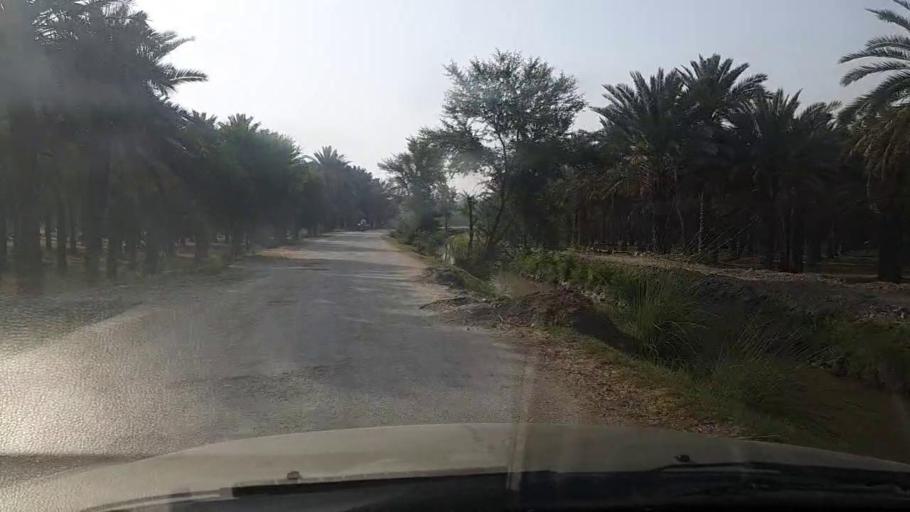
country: PK
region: Sindh
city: Pir jo Goth
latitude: 27.5597
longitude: 68.5452
